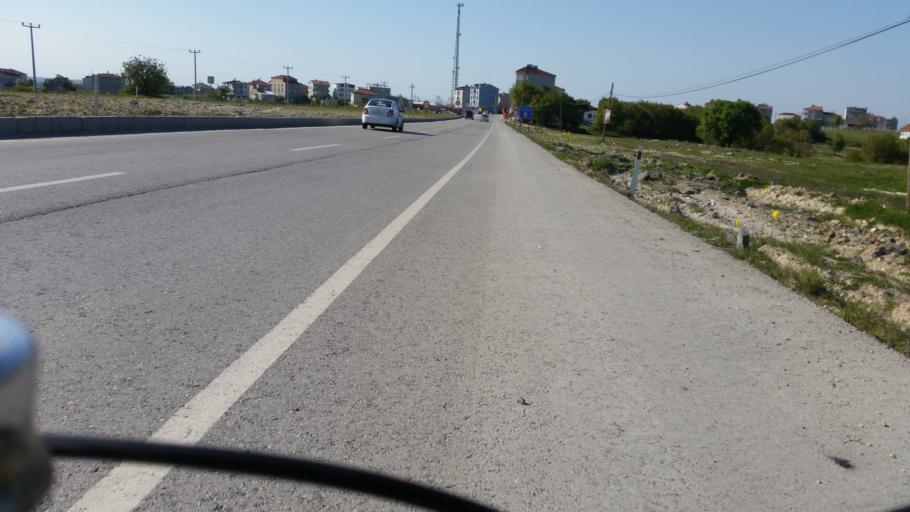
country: TR
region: Tekirdag
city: Cerkezkoey
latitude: 41.3533
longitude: 27.9562
